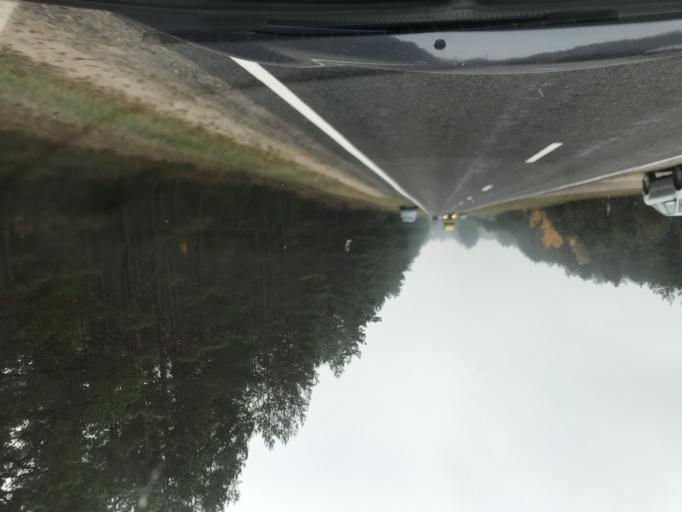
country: BY
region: Grodnenskaya
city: Hrodna
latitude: 53.8538
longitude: 23.8915
